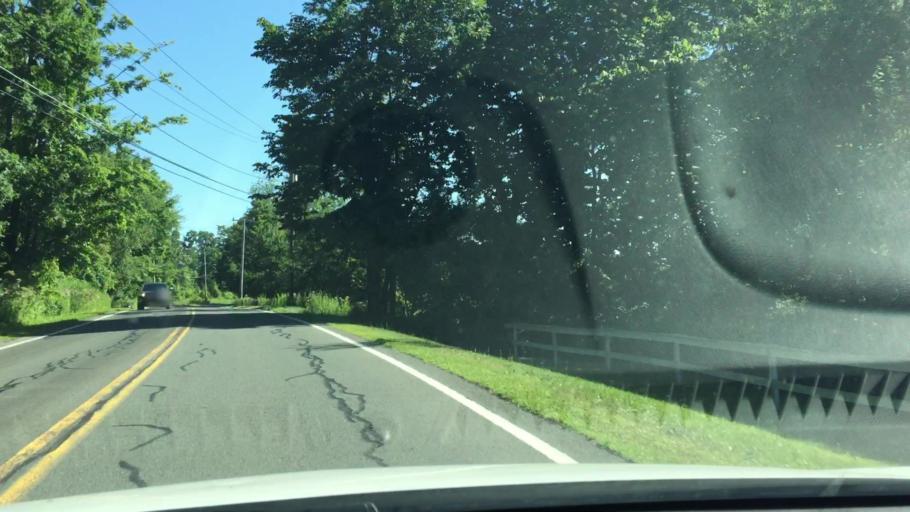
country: US
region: Massachusetts
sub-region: Berkshire County
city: Lenox
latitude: 42.4170
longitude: -73.3107
